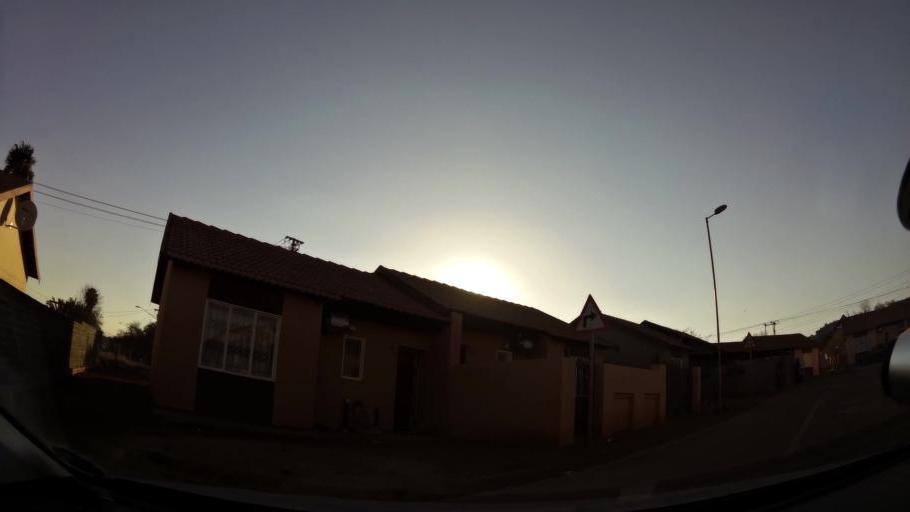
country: ZA
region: Gauteng
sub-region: City of Tshwane Metropolitan Municipality
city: Pretoria
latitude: -25.7371
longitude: 28.1203
